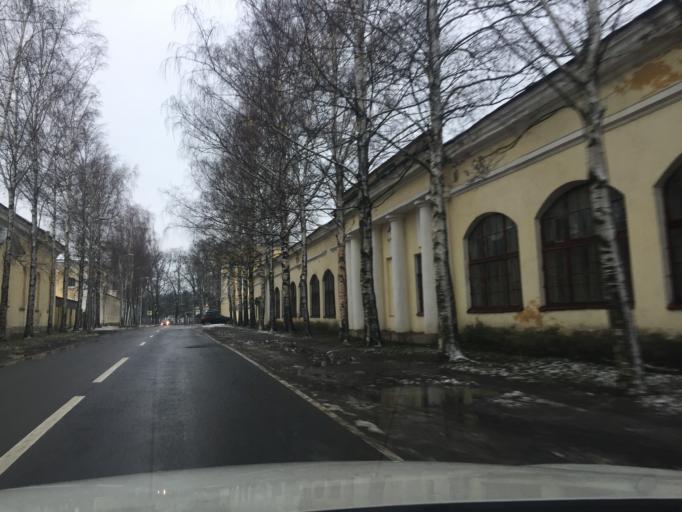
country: RU
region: St.-Petersburg
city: Pushkin
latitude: 59.7073
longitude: 30.3947
